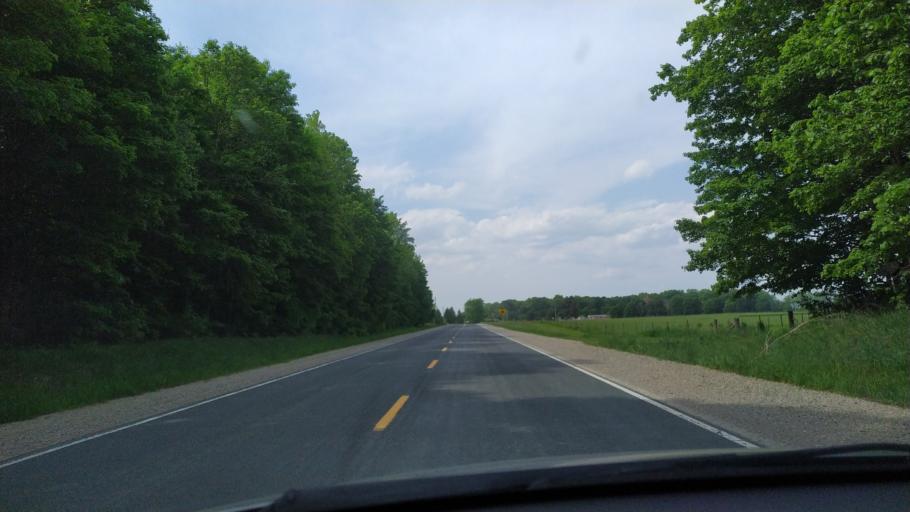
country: CA
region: Ontario
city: Ingersoll
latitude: 43.0446
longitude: -80.9803
